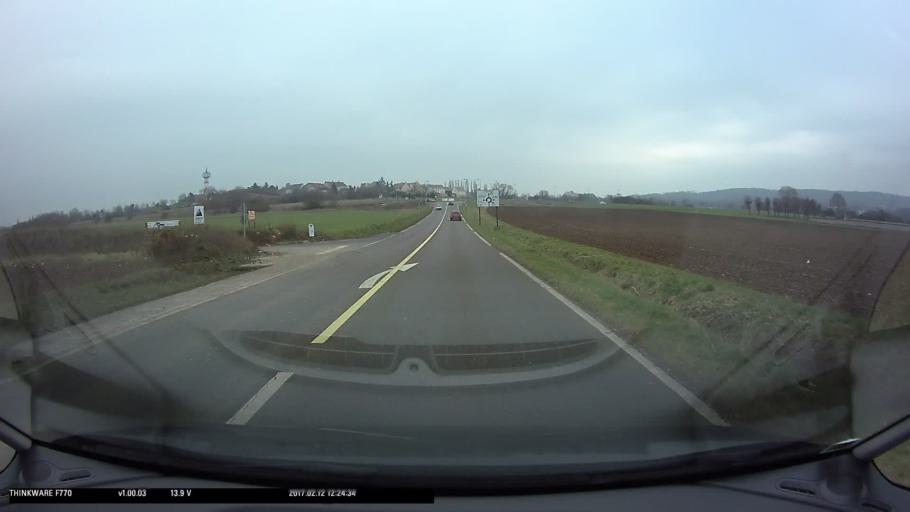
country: FR
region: Ile-de-France
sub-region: Departement du Val-d'Oise
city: Courdimanche
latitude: 49.0392
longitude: 1.9943
